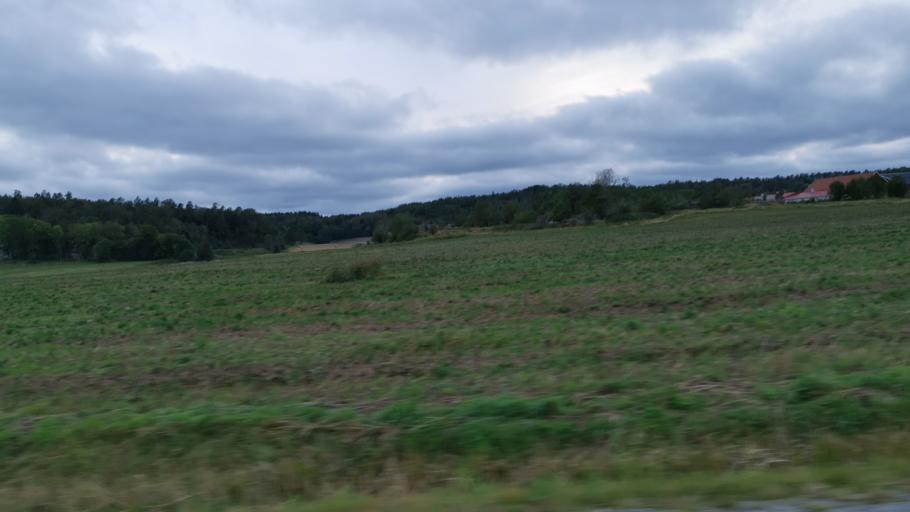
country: SE
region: Vaestra Goetaland
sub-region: Tanums Kommun
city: Tanumshede
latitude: 58.6665
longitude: 11.3440
